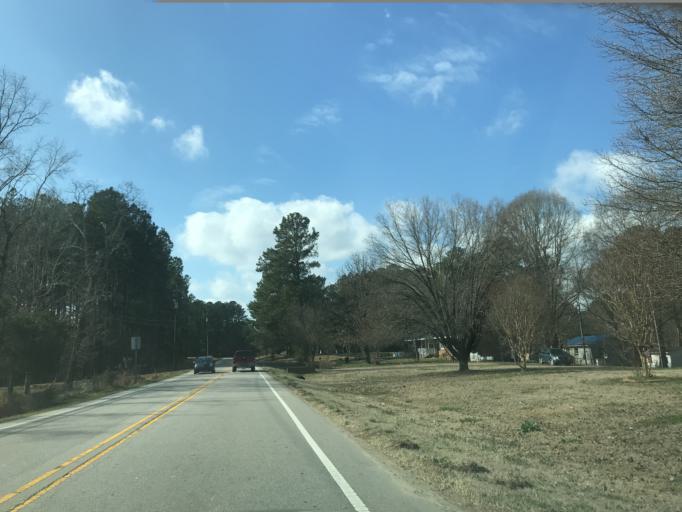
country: US
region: North Carolina
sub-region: Durham County
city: Gorman
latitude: 35.9617
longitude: -78.8113
